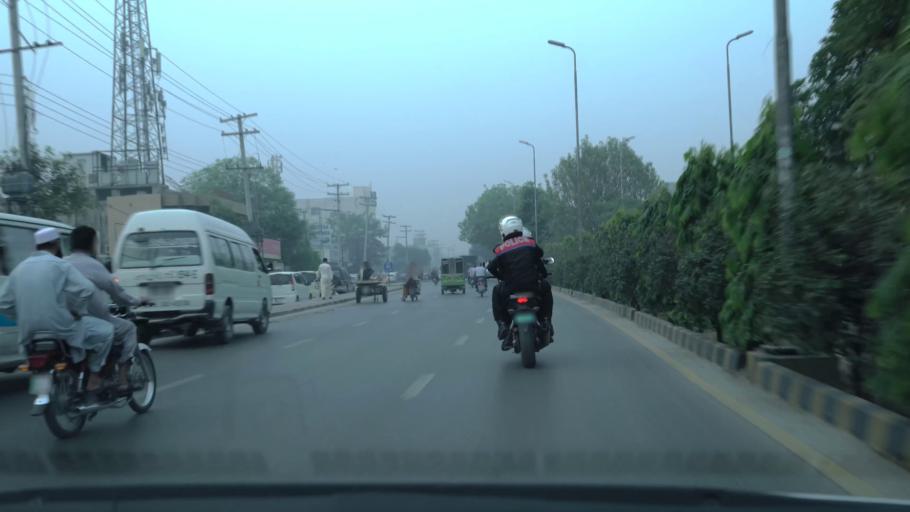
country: PK
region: Punjab
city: Lahore
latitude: 31.4751
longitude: 74.3019
